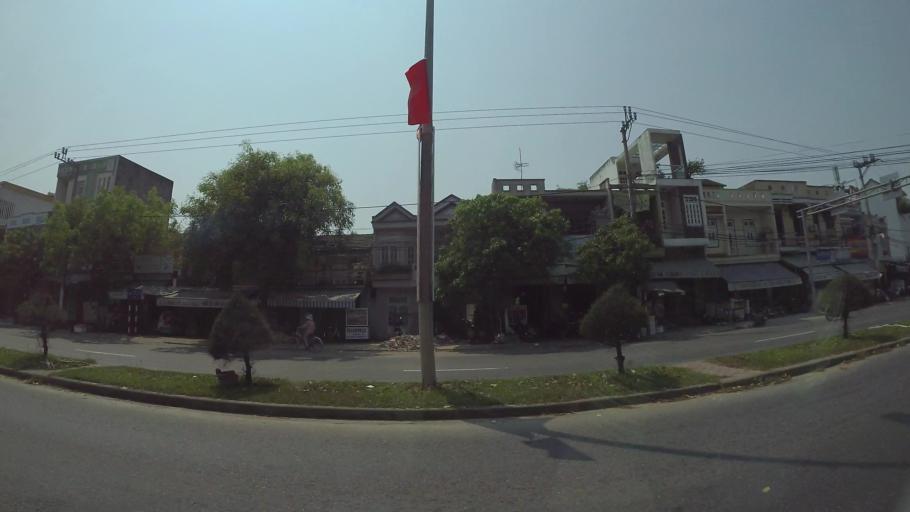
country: VN
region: Da Nang
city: Cam Le
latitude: 15.9799
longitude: 108.2082
